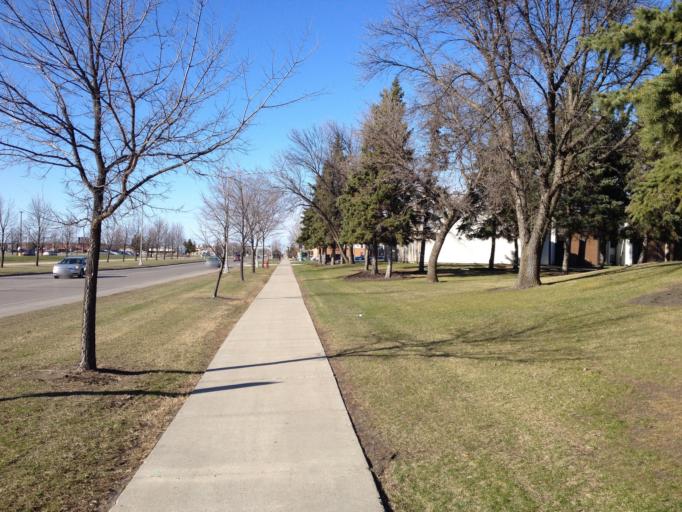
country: US
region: North Dakota
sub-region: Cass County
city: Fargo
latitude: 46.9013
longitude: -96.7979
